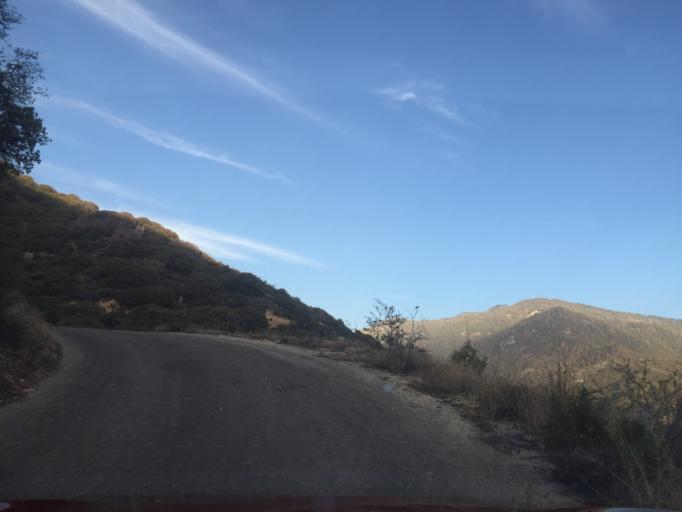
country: US
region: California
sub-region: Tulare County
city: Three Rivers
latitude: 36.4335
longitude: -118.7442
